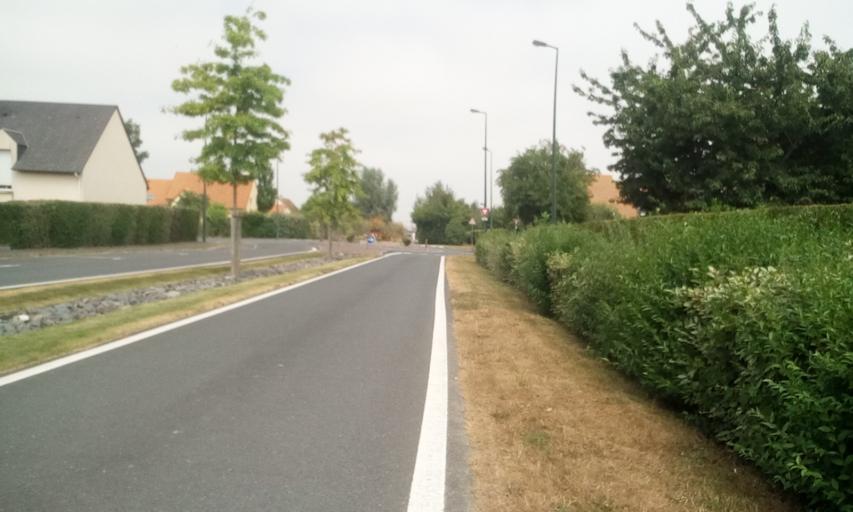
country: FR
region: Lower Normandy
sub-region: Departement du Calvados
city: Douvres-la-Delivrande
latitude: 49.2986
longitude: -0.3857
